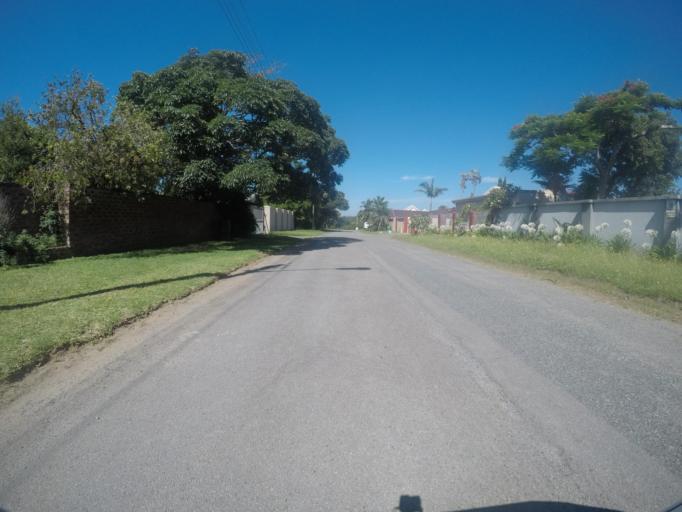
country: ZA
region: Eastern Cape
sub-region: Buffalo City Metropolitan Municipality
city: East London
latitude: -32.9494
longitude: 28.0039
